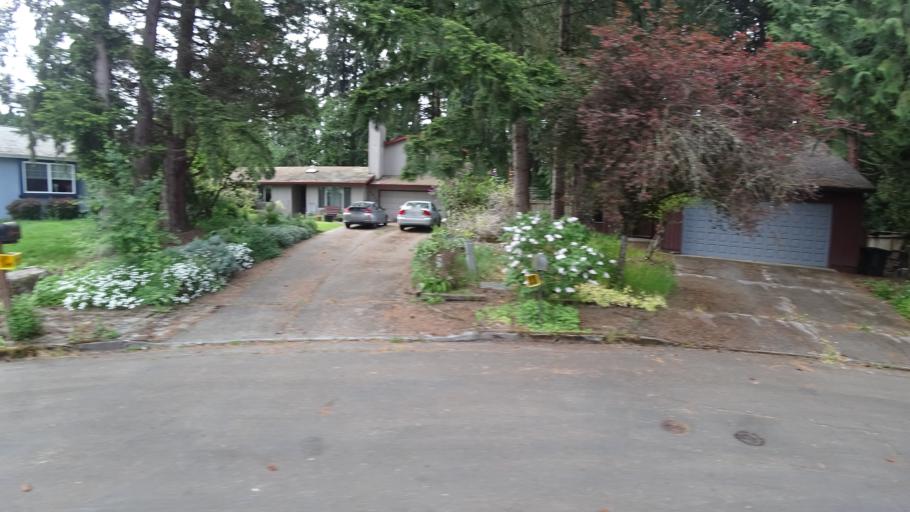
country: US
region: Oregon
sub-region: Washington County
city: Aloha
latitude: 45.5129
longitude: -122.8756
